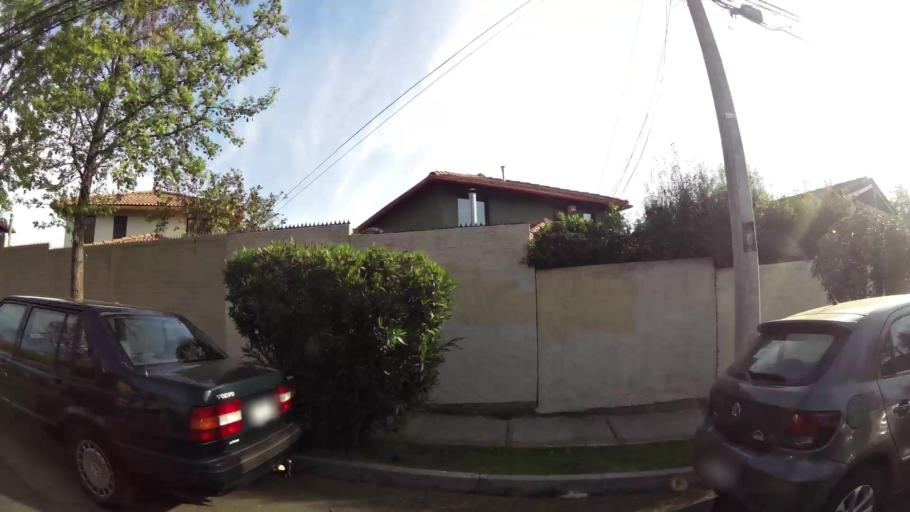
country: CL
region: Santiago Metropolitan
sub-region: Provincia de Santiago
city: Villa Presidente Frei, Nunoa, Santiago, Chile
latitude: -33.5101
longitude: -70.5588
